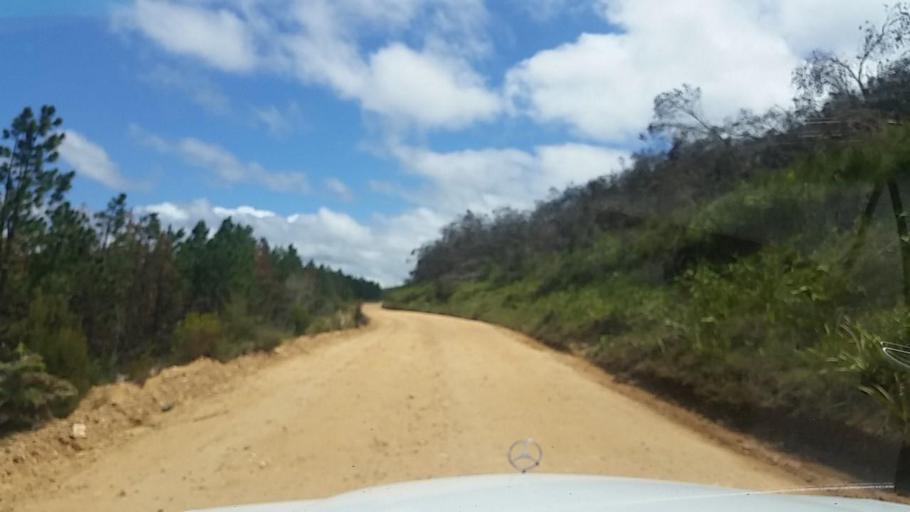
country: ZA
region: Western Cape
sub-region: Eden District Municipality
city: Knysna
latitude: -33.8917
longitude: 23.1677
